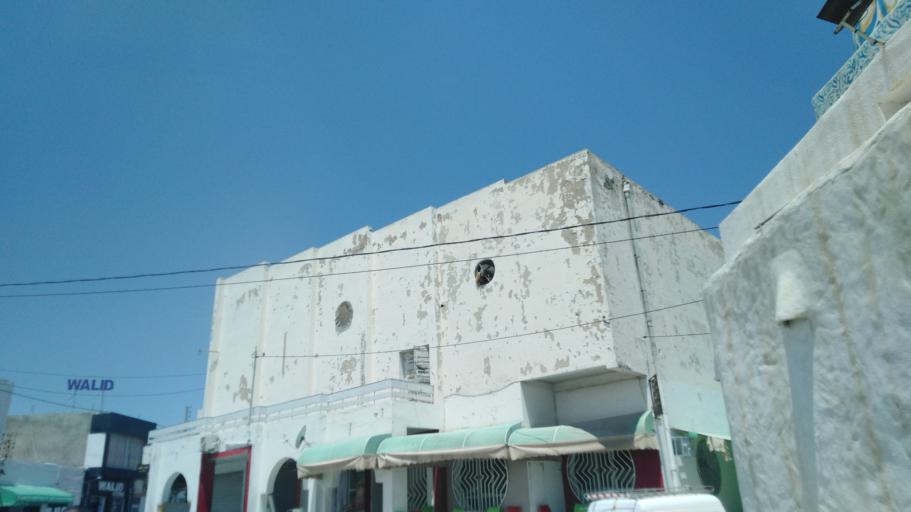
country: TN
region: Al Mahdiyah
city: Ksour Essaf
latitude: 35.4171
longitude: 10.9925
